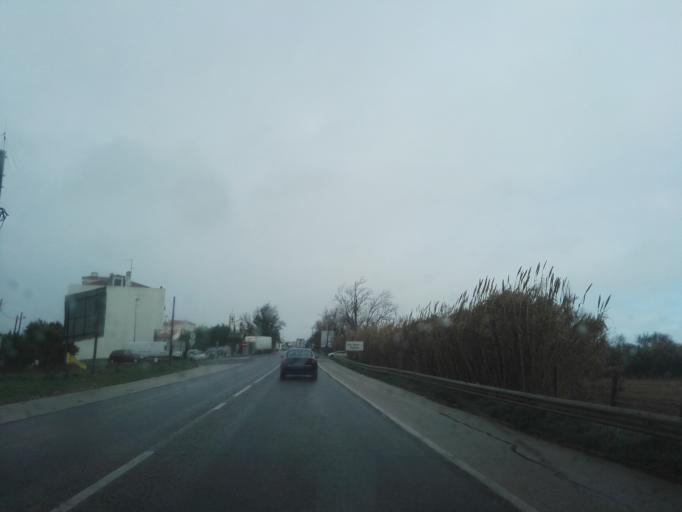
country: PT
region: Lisbon
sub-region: Alenquer
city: Carregado
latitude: 39.0346
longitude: -8.9379
